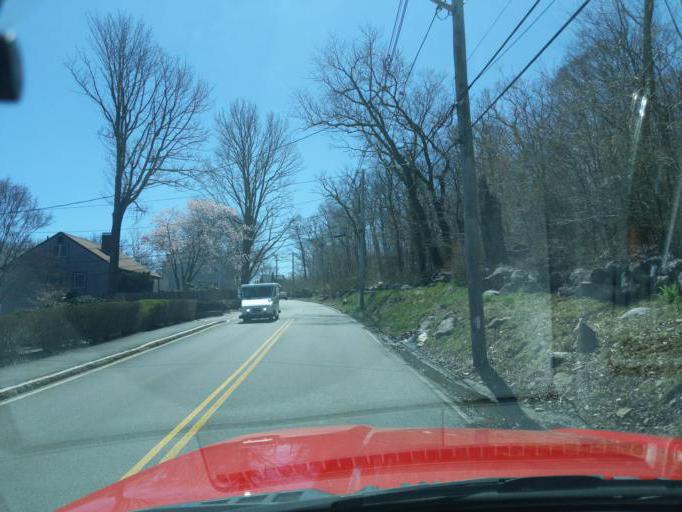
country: US
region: Massachusetts
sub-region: Essex County
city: Rockport
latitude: 42.6605
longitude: -70.6266
